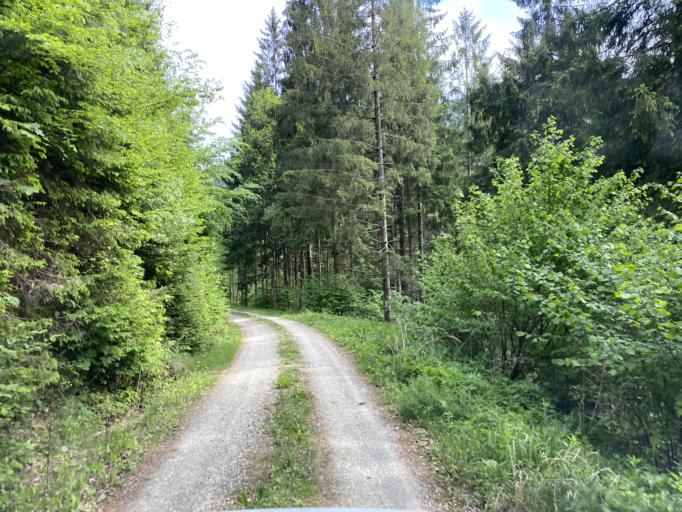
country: AT
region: Styria
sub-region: Politischer Bezirk Weiz
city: Koglhof
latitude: 47.3153
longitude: 15.6481
